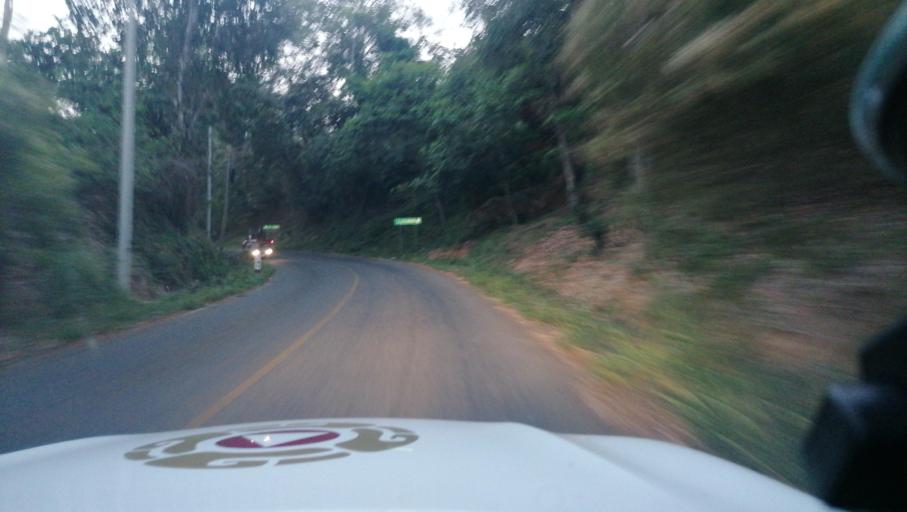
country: MX
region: Chiapas
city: Veinte de Noviembre
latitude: 15.0082
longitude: -92.2466
